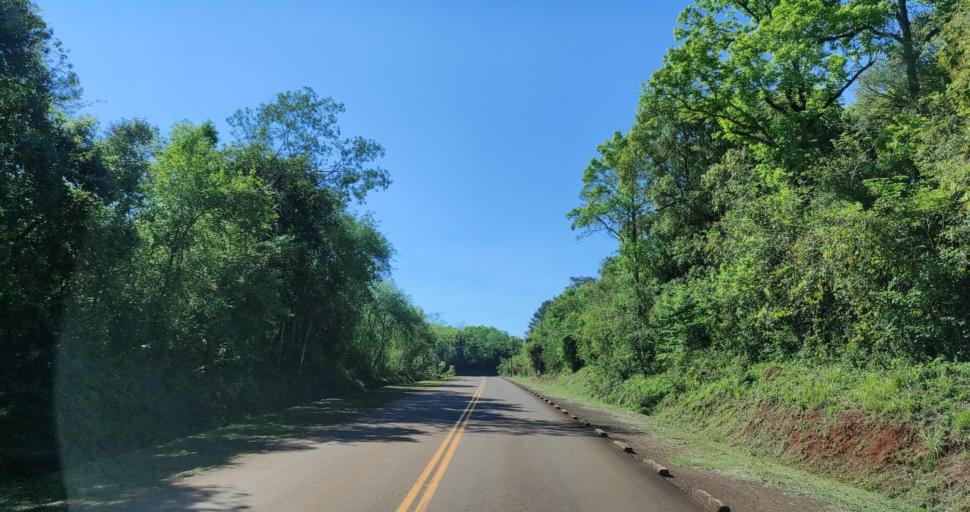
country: AR
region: Misiones
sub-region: Departamento de Candelaria
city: Loreto
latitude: -27.3377
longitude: -55.5326
